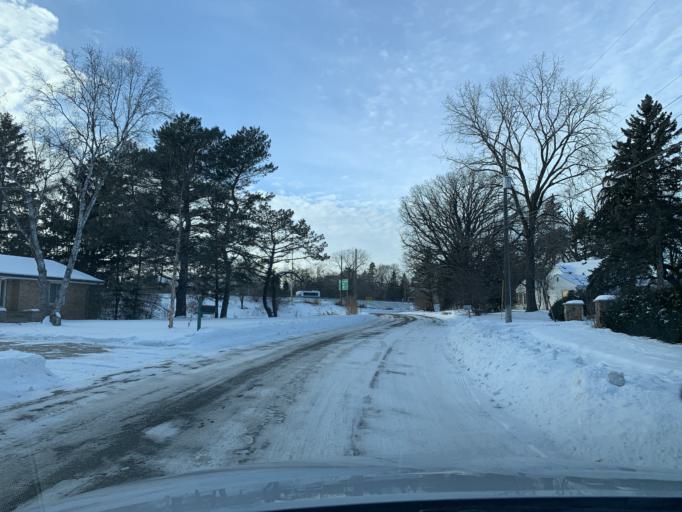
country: US
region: Minnesota
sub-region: Hennepin County
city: Minnetonka Mills
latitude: 44.9506
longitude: -93.3991
